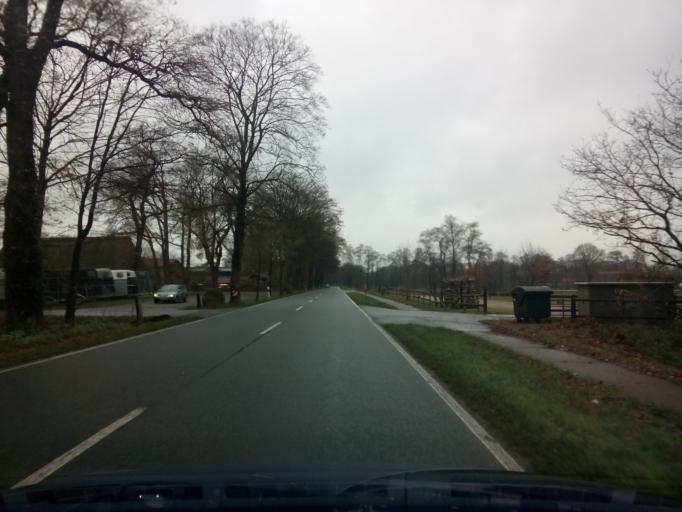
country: DE
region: Lower Saxony
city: Lilienthal
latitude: 53.1789
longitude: 8.8819
